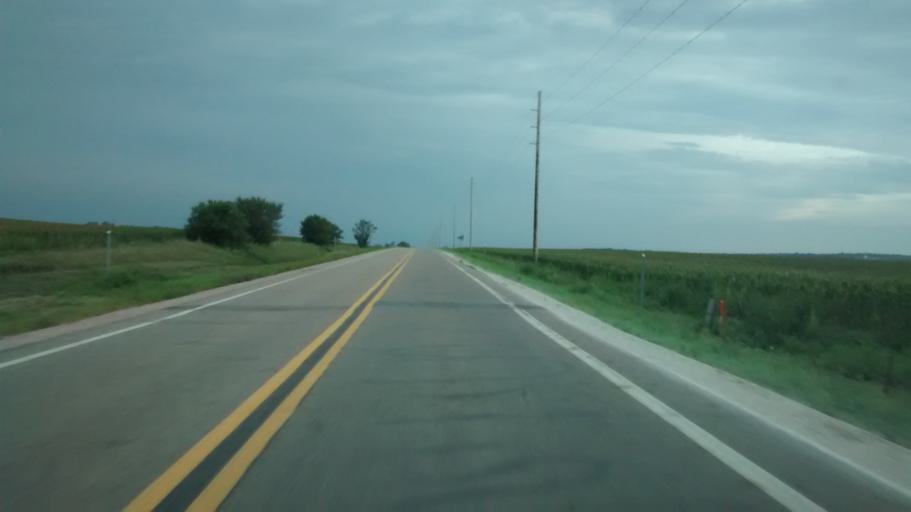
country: US
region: Iowa
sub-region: Plymouth County
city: Kingsley
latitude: 42.5817
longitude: -95.9839
